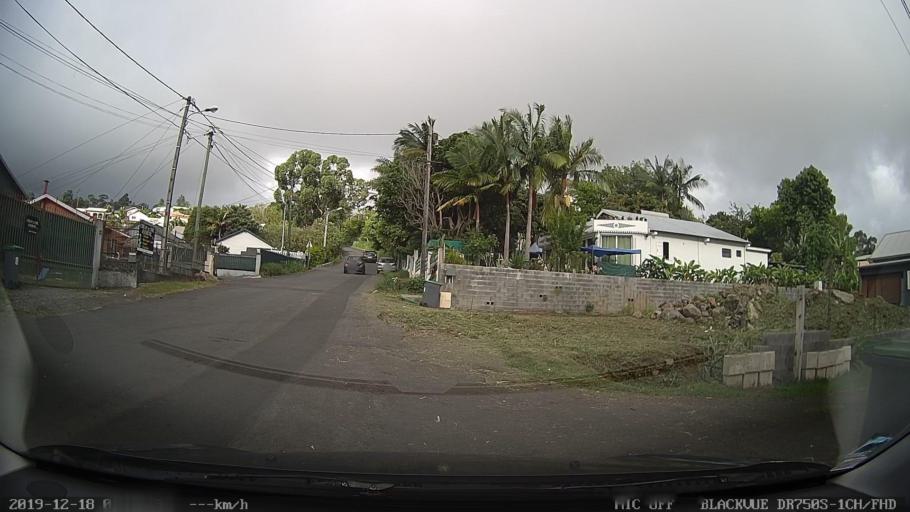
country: RE
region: Reunion
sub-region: Reunion
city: Le Tampon
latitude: -21.2578
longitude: 55.5149
